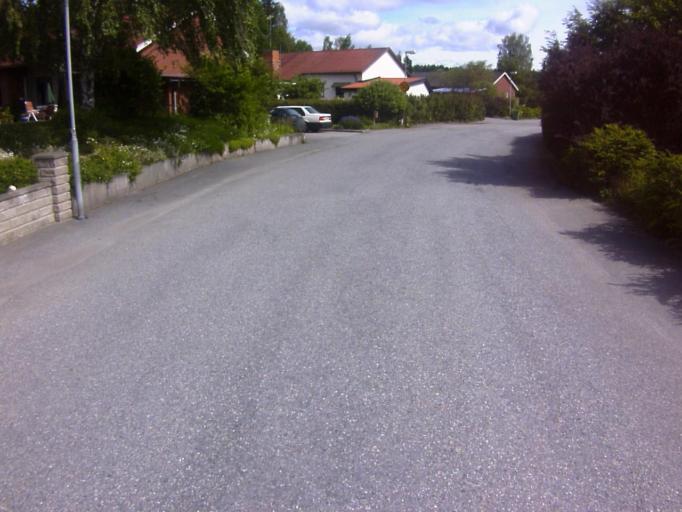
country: SE
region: Soedermanland
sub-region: Eskilstuna Kommun
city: Skogstorp
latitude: 59.3225
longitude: 16.4902
